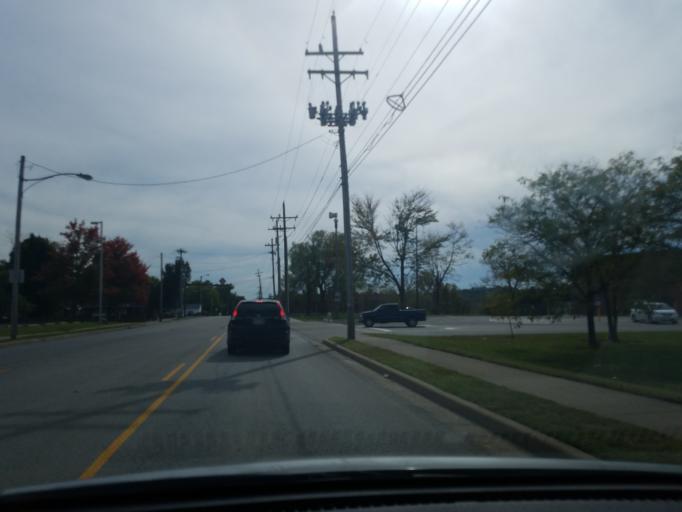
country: US
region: Indiana
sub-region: Floyd County
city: New Albany
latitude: 38.3061
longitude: -85.8366
